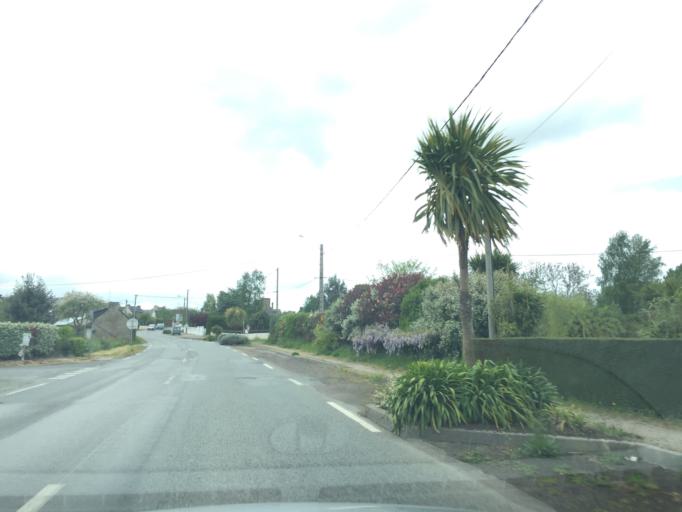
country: FR
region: Brittany
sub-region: Departement des Cotes-d'Armor
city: Crehen
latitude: 48.5808
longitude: -2.2300
